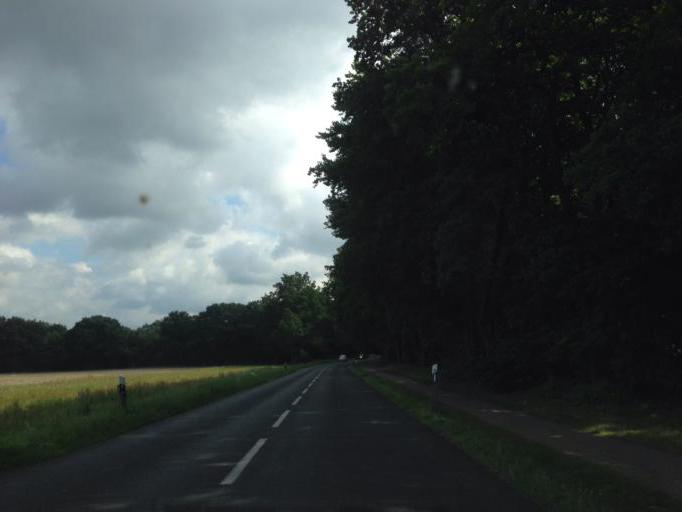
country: DE
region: Lower Saxony
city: Adendorf
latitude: 53.2969
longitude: 10.4544
